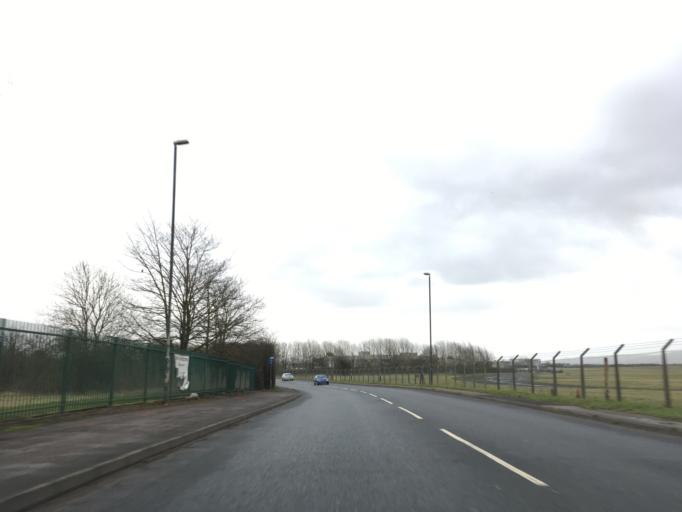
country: GB
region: England
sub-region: Gloucestershire
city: Churchdown
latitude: 51.8986
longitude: -2.1690
